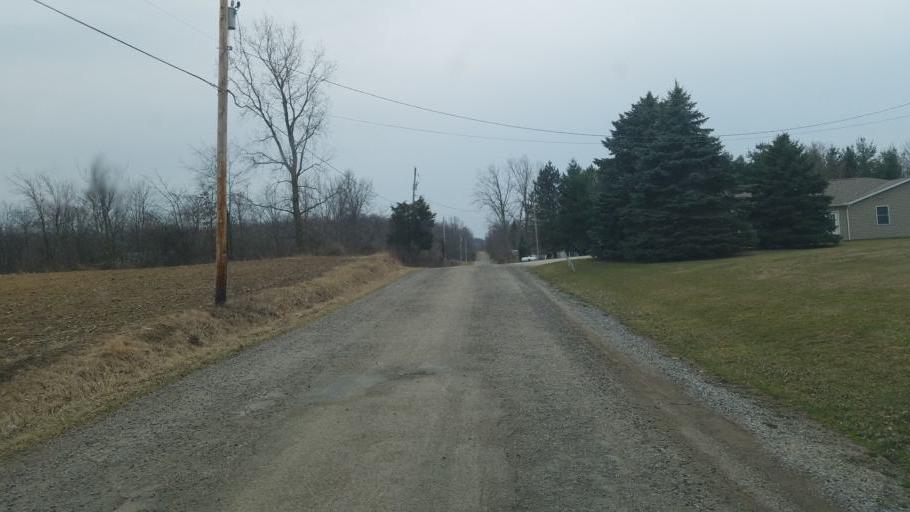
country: US
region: Ohio
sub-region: Crawford County
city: Galion
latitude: 40.6599
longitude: -82.7941
